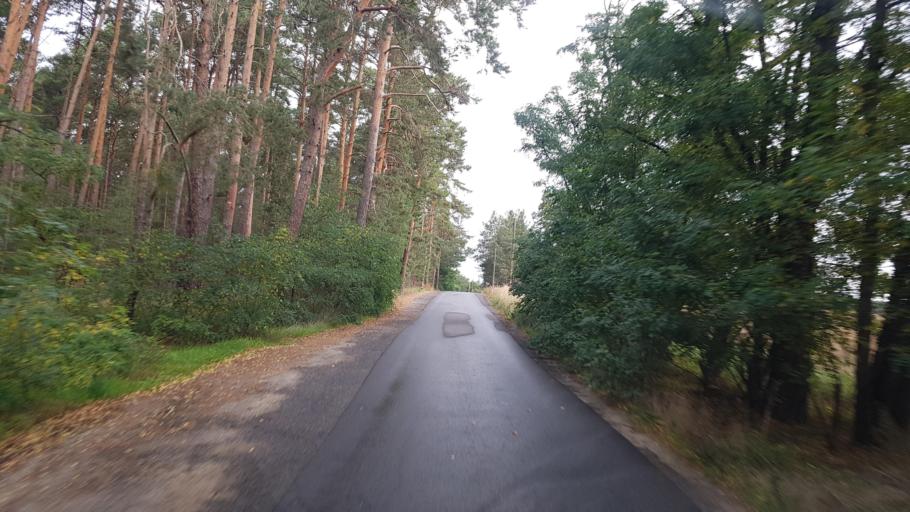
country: DE
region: Brandenburg
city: Kasel-Golzig
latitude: 51.9316
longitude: 13.7464
